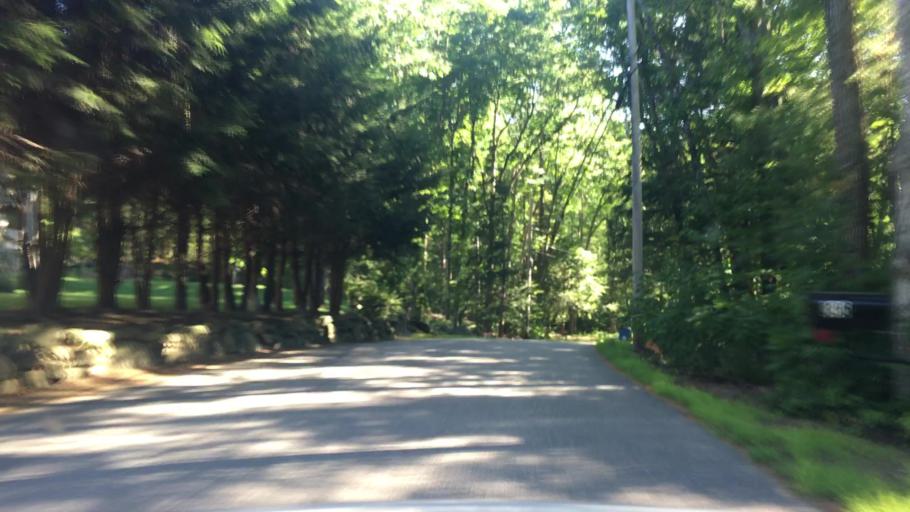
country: US
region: New Hampshire
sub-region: Rockingham County
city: Exeter
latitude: 43.0106
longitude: -70.9790
